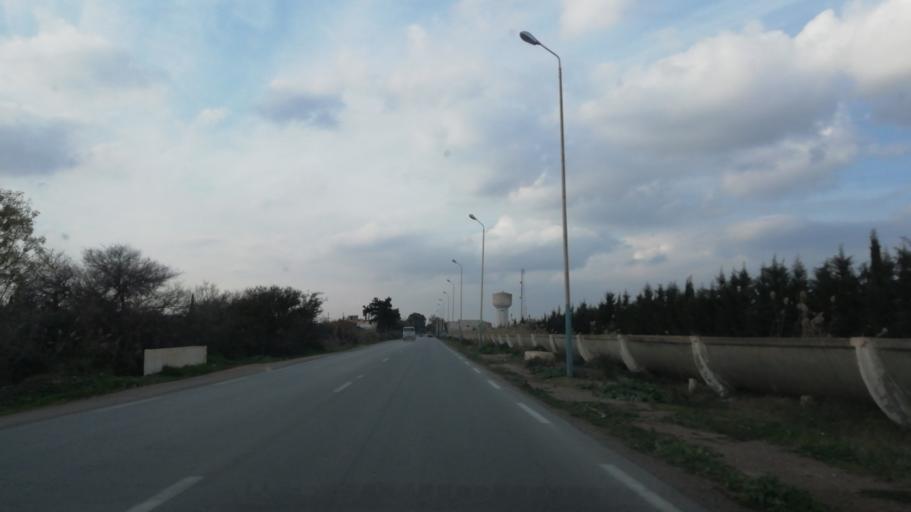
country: DZ
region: Mascara
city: Sig
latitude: 35.6535
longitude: 0.0186
